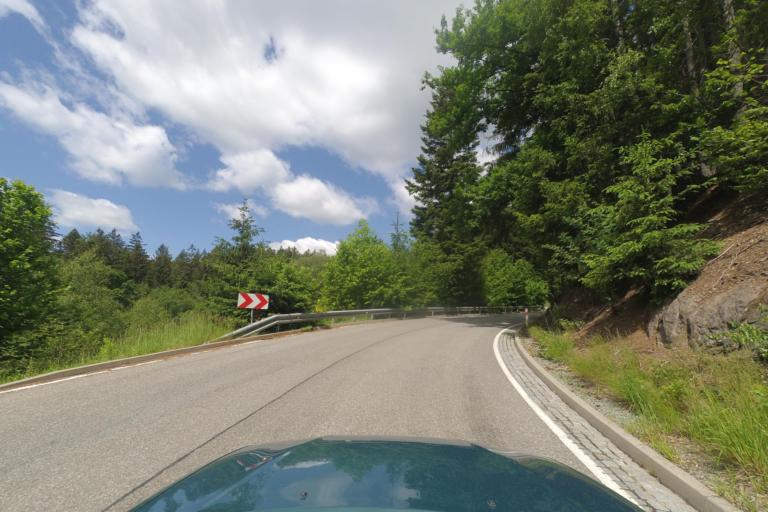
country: PL
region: Lower Silesian Voivodeship
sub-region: Powiat klodzki
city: Lewin Klodzki
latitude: 50.3498
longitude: 16.2391
